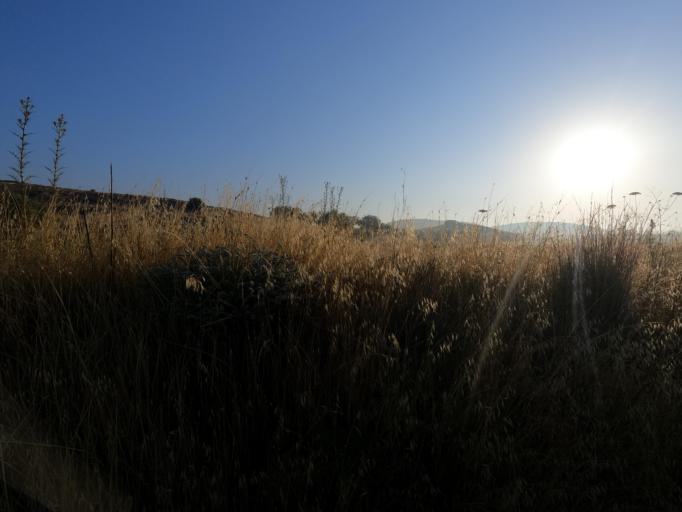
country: CY
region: Larnaka
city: Mosfiloti
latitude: 34.9733
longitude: 33.4250
